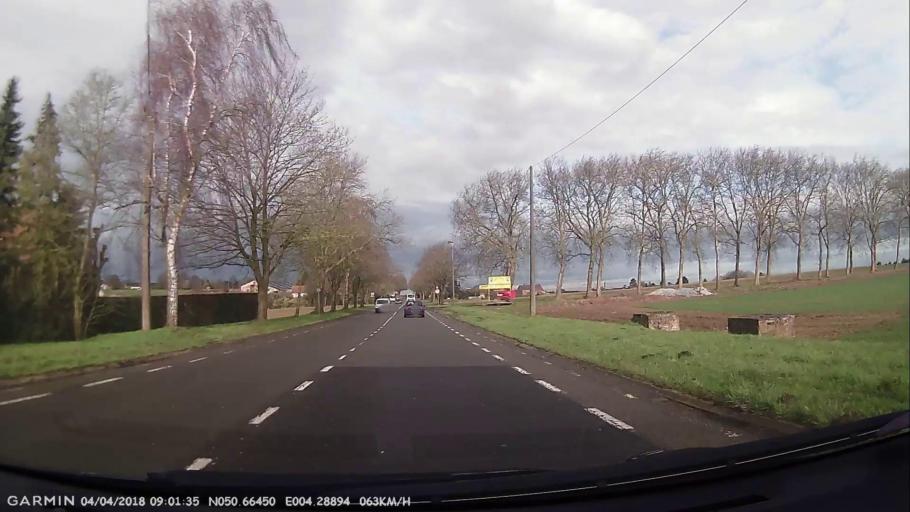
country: BE
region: Wallonia
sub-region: Province du Brabant Wallon
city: Braine-le-Chateau
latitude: 50.6646
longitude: 4.2885
